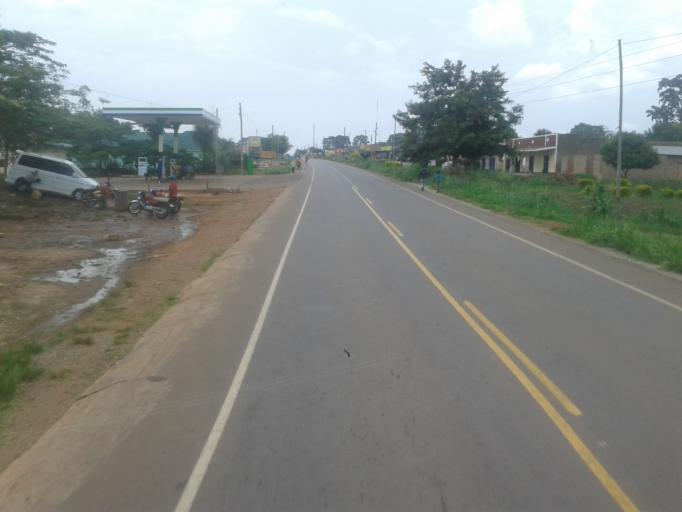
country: UG
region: Western Region
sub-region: Kiryandongo District
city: Kiryandongo
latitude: 1.8698
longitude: 32.0540
